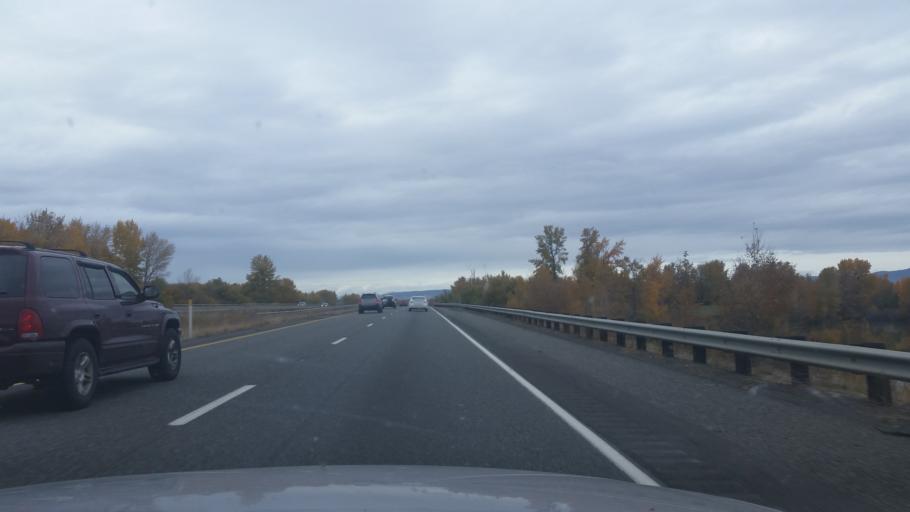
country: US
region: Washington
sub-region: Kittitas County
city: Ellensburg
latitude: 47.0188
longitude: -120.6077
